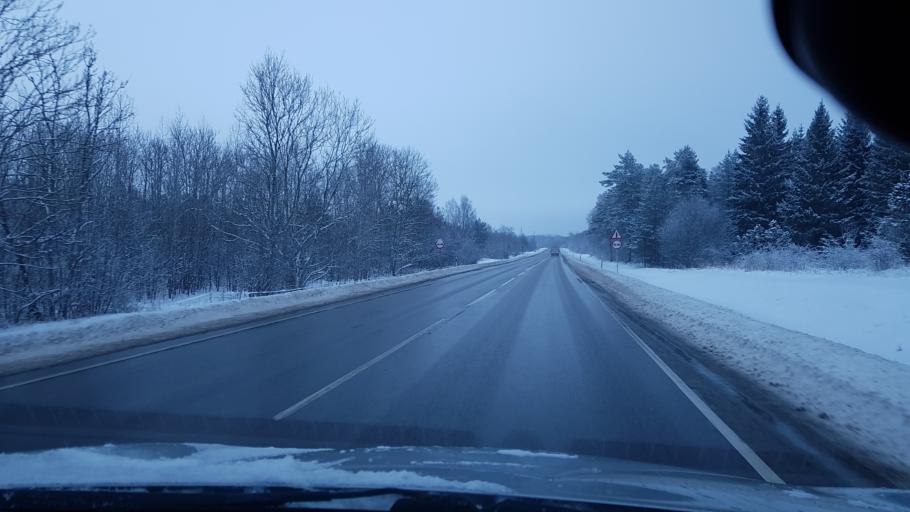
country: EE
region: Harju
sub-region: Saue linn
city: Saue
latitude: 59.3649
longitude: 24.5065
